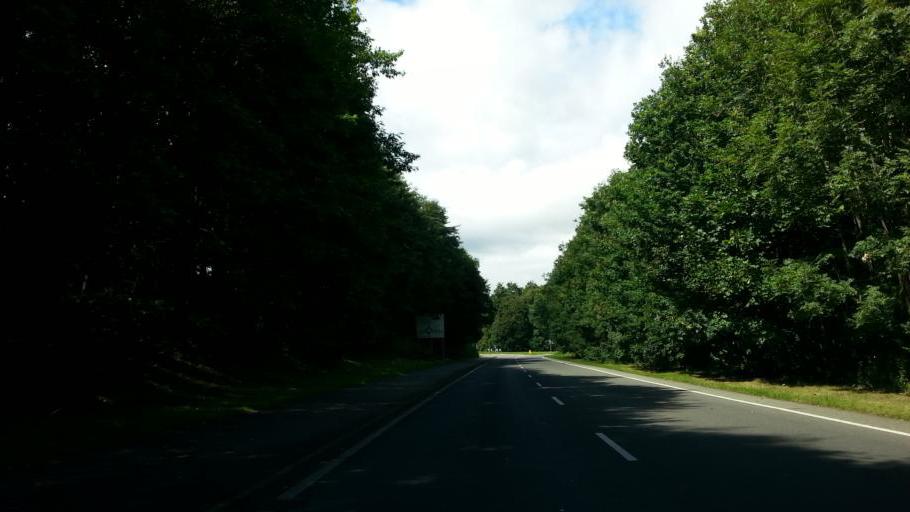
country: GB
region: England
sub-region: Northamptonshire
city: Northampton
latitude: 52.2734
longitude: -0.8240
